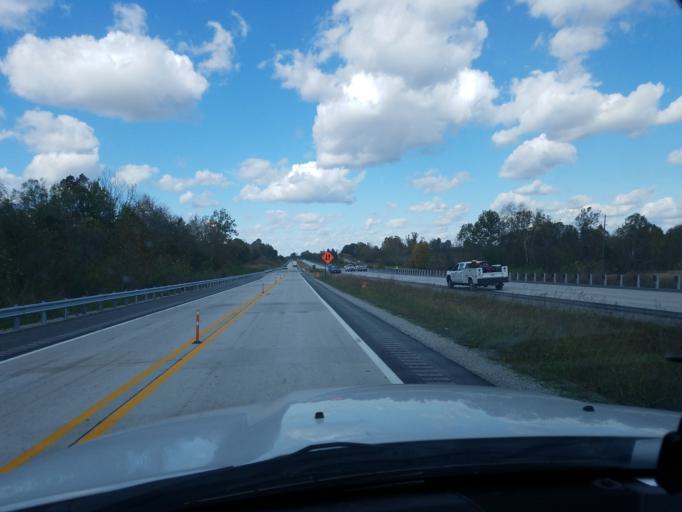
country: US
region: Kentucky
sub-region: Ohio County
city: Beaver Dam
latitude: 37.4177
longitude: -86.8344
